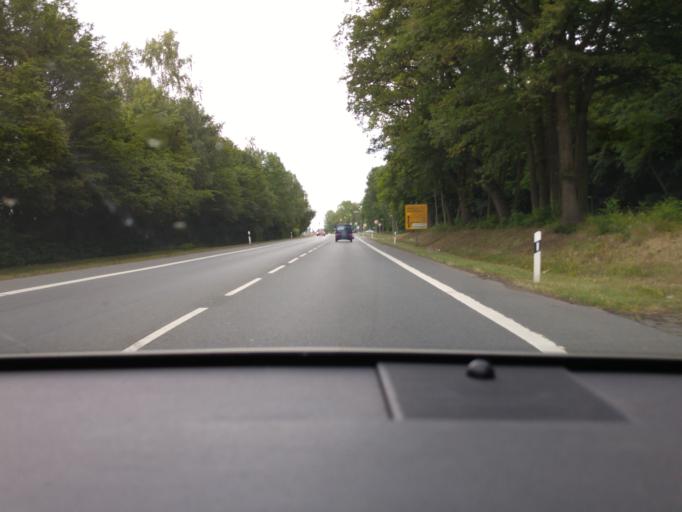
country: DE
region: Hesse
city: Dreieich
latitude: 50.0042
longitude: 8.6841
